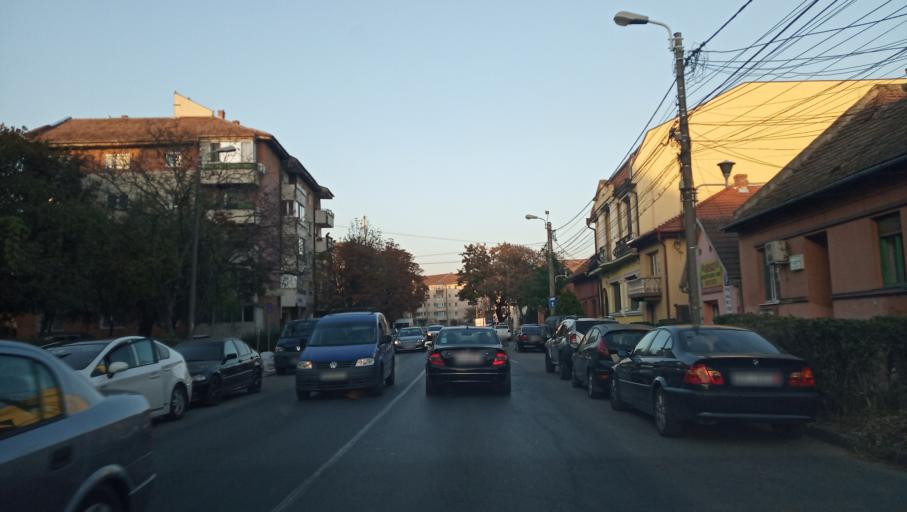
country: RO
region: Timis
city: Timisoara
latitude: 45.7537
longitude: 21.2528
